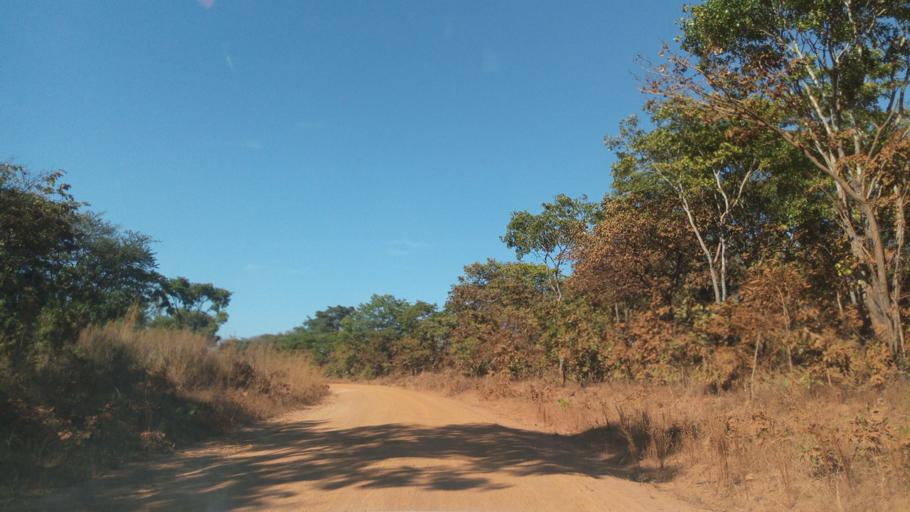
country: ZM
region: Luapula
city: Mwense
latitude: -10.6588
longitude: 28.4076
